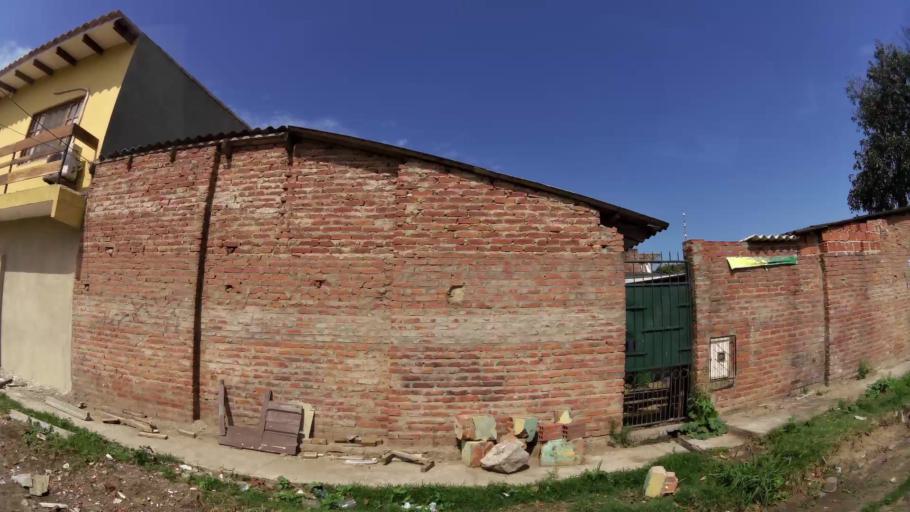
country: BO
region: Santa Cruz
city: Santa Cruz de la Sierra
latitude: -17.7462
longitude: -63.1588
